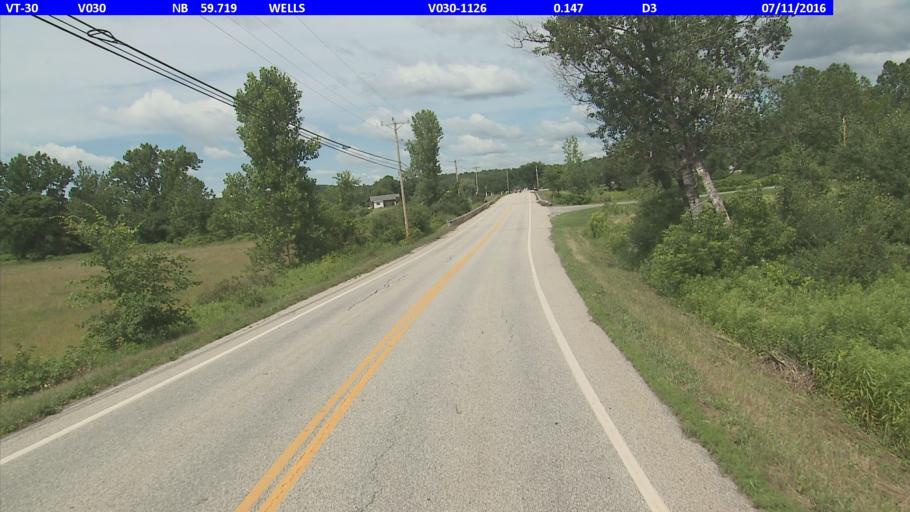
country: US
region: New York
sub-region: Washington County
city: Granville
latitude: 43.4098
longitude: -73.2262
